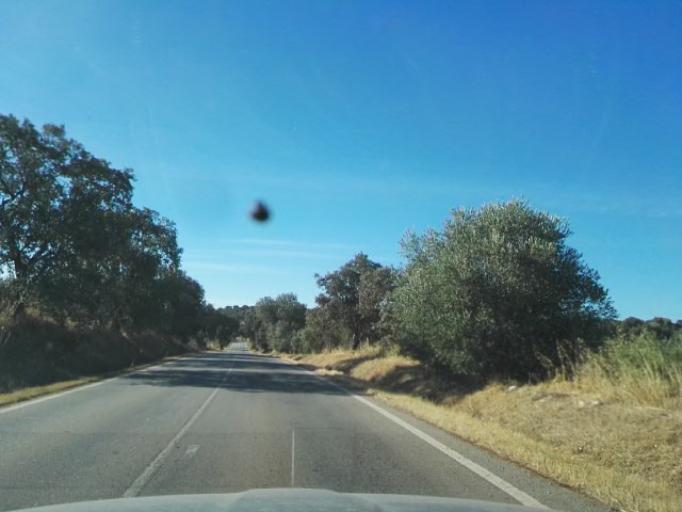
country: PT
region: Portalegre
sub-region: Elvas
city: Elvas
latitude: 38.9159
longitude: -7.1823
